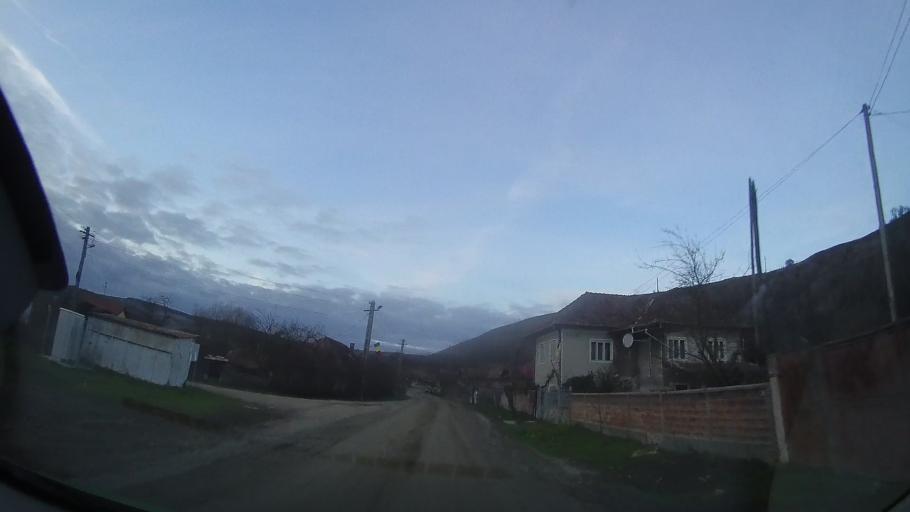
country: RO
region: Cluj
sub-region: Comuna Palatca
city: Palatca
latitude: 46.8660
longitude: 24.0169
